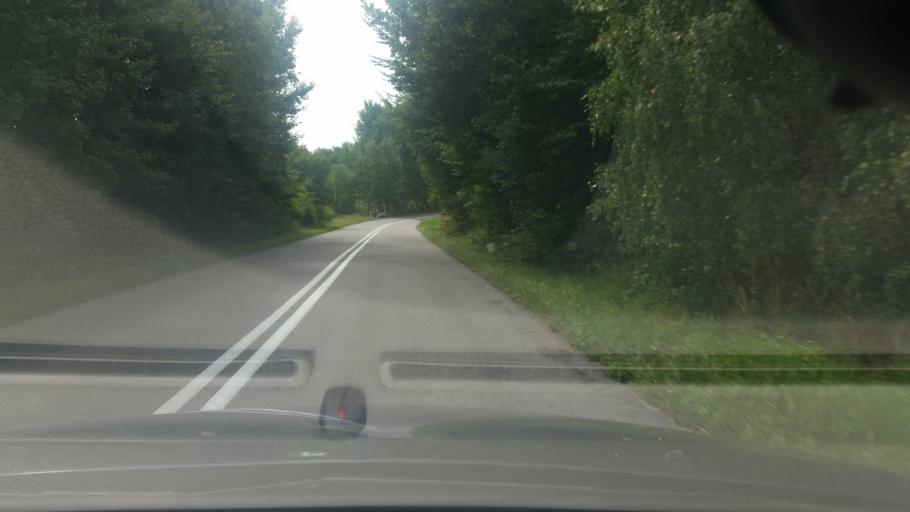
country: PL
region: Pomeranian Voivodeship
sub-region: Powiat leborski
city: Leba
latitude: 54.7473
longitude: 17.6630
